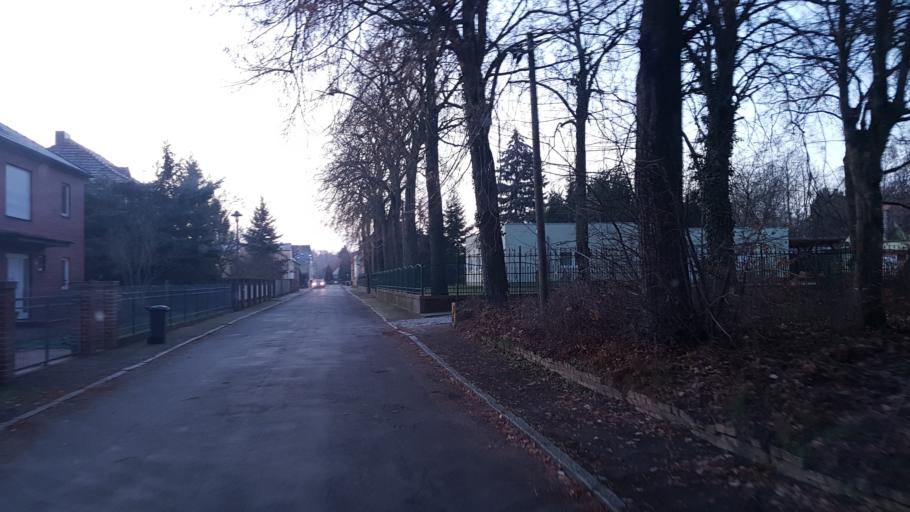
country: DE
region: Brandenburg
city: Schipkau
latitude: 51.5429
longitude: 13.8919
